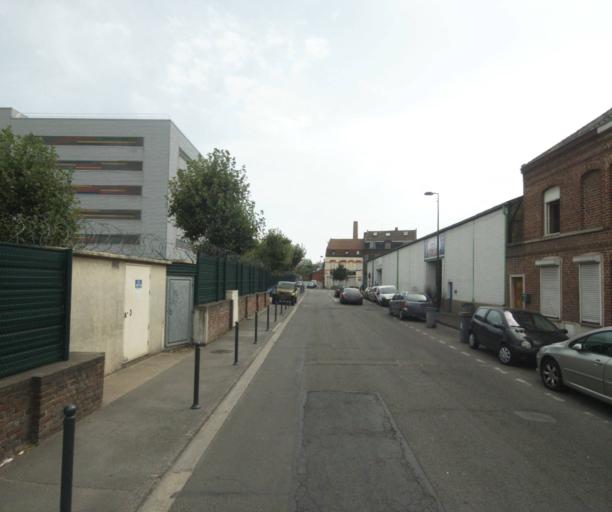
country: FR
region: Nord-Pas-de-Calais
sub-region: Departement du Nord
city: Wattrelos
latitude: 50.6916
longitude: 3.2002
